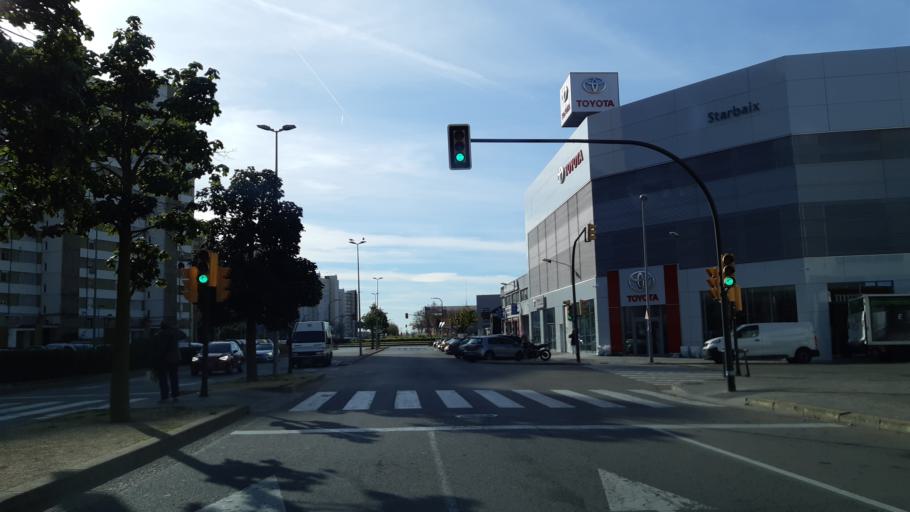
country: ES
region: Catalonia
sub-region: Provincia de Barcelona
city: L'Hospitalet de Llobregat
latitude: 41.3543
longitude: 2.1087
